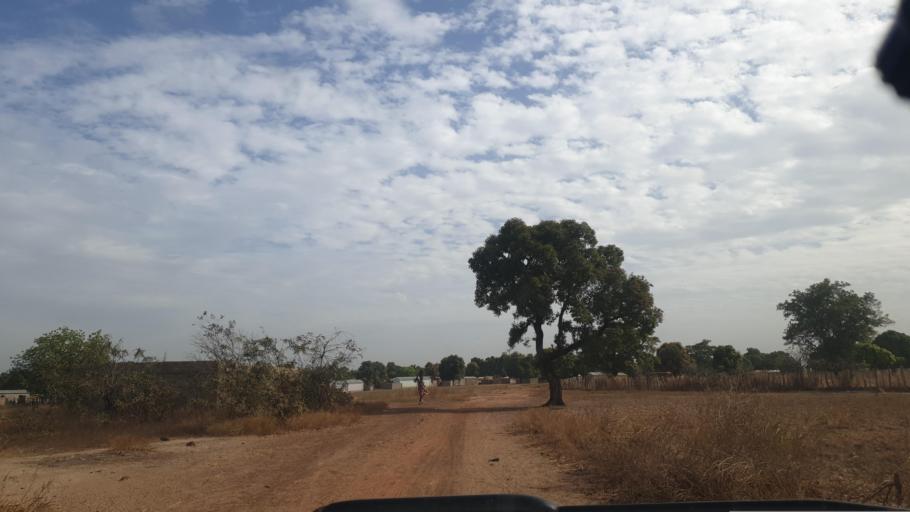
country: ML
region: Sikasso
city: Yanfolila
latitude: 11.4139
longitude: -8.0029
